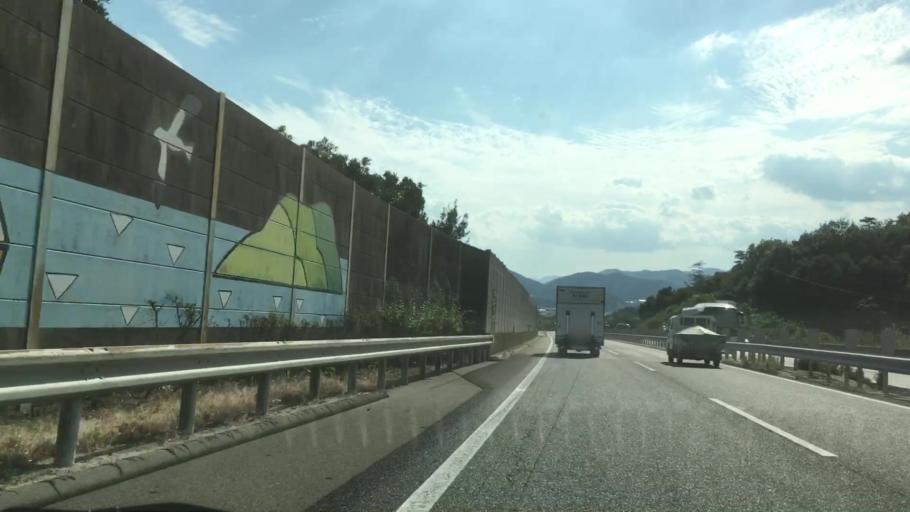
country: JP
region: Hiroshima
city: Ono-hara
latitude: 34.2697
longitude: 132.2441
